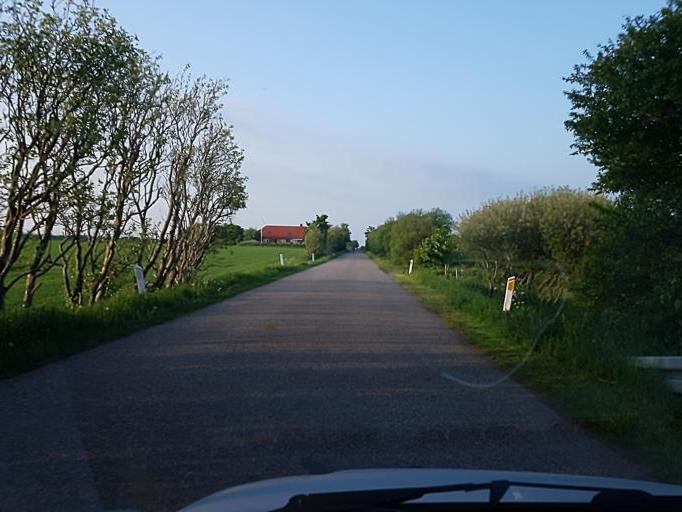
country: DK
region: South Denmark
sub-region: Esbjerg Kommune
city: Tjaereborg
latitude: 55.5511
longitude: 8.5449
